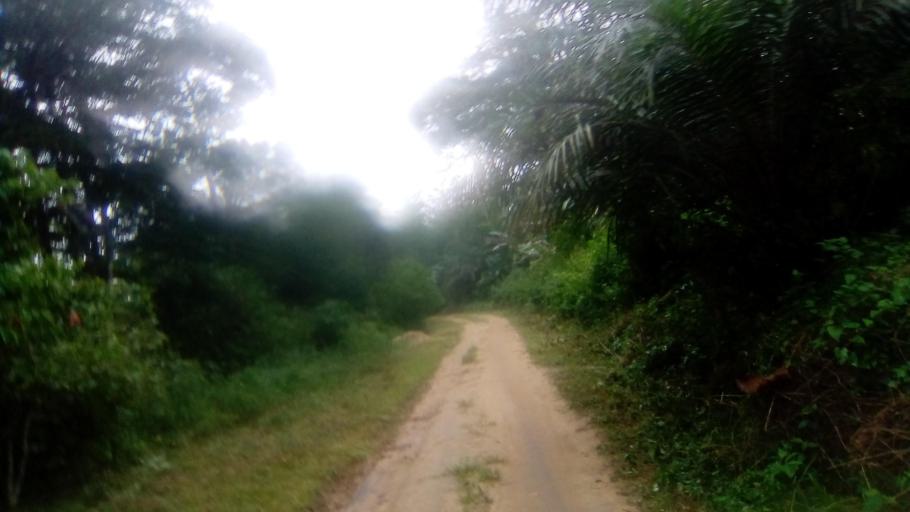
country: SL
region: Eastern Province
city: Kailahun
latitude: 8.2943
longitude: -10.6016
